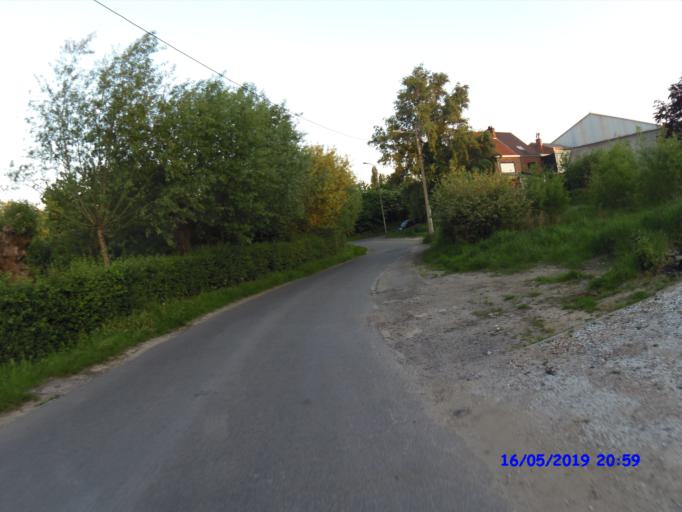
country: BE
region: Flanders
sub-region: Provincie West-Vlaanderen
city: Kuurne
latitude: 50.8331
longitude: 3.2873
